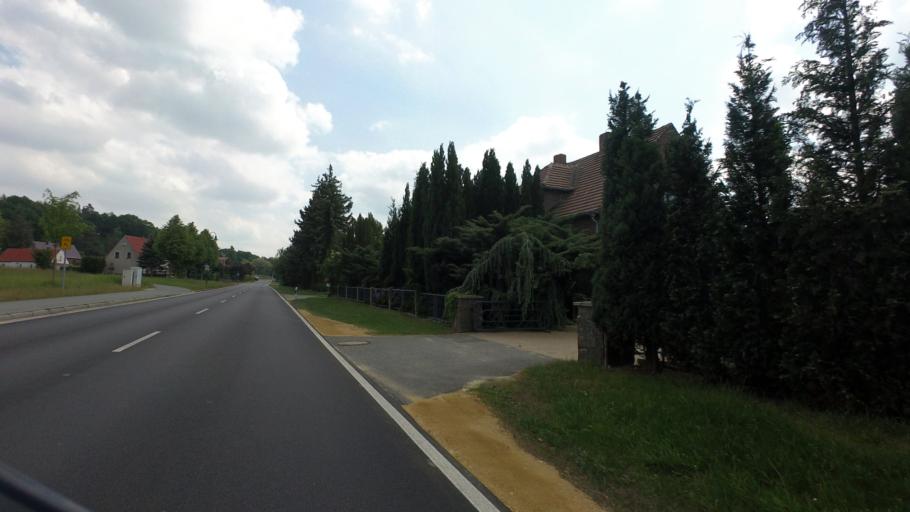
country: DE
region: Saxony
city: Rietschen
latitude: 51.3631
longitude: 14.8012
